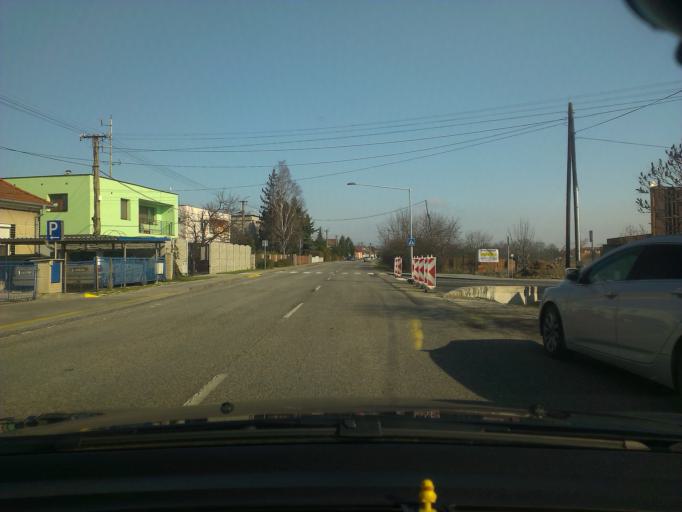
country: SK
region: Nitriansky
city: Cachtice
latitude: 48.6836
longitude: 17.8472
